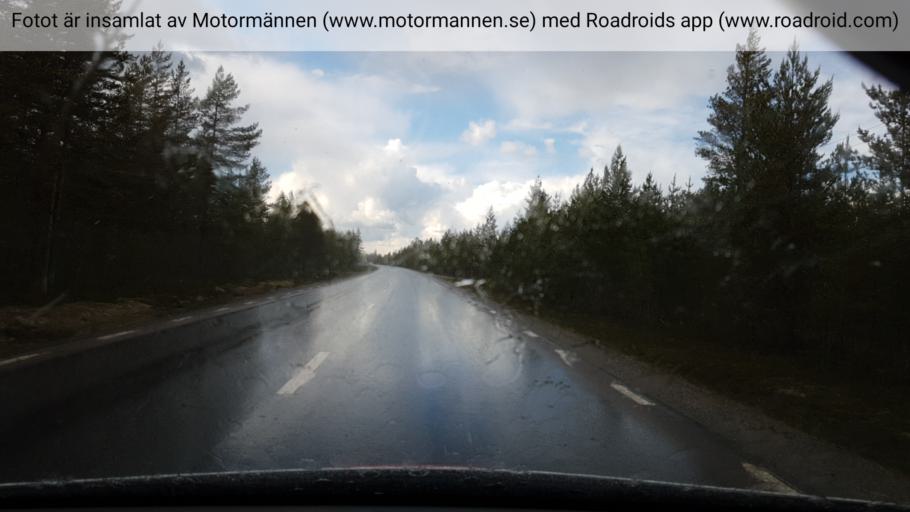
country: SE
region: Vaesterbotten
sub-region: Umea Kommun
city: Roback
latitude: 63.9613
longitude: 20.1306
